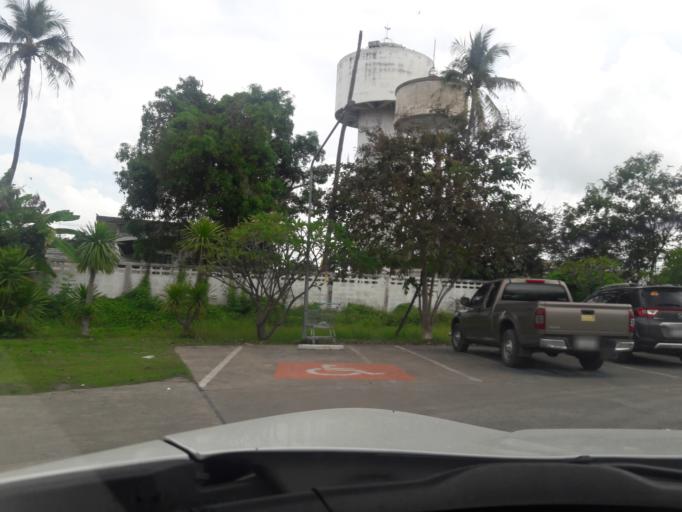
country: TH
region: Lop Buri
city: Ban Mi
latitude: 15.0455
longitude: 100.5488
